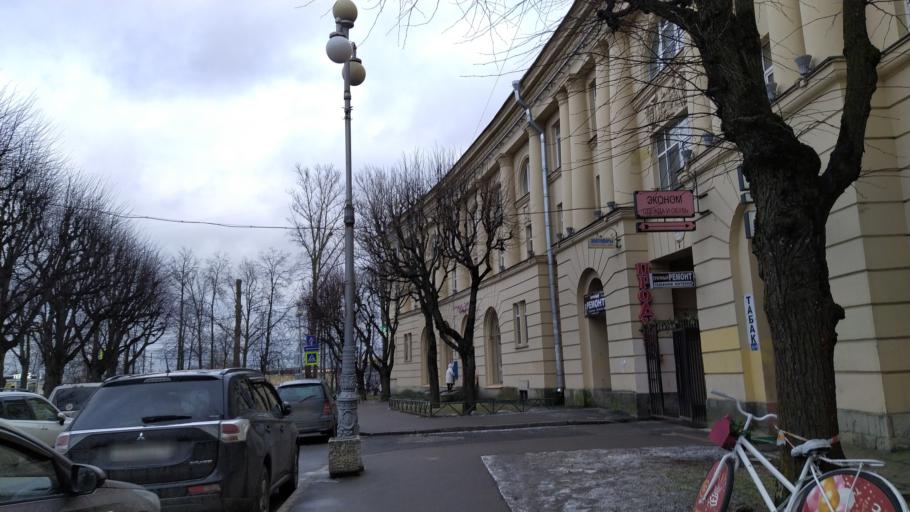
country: RU
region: St.-Petersburg
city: Pushkin
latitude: 59.7220
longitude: 30.4279
